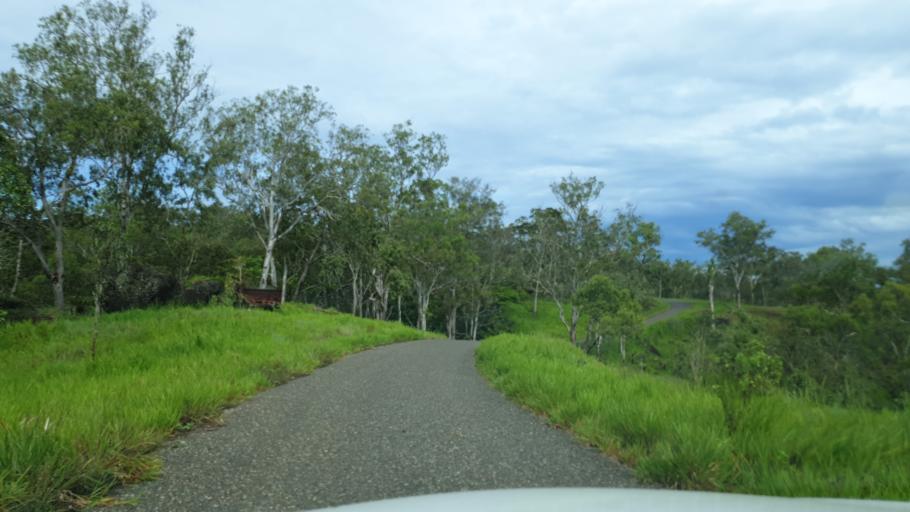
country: PG
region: National Capital
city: Port Moresby
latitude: -9.4352
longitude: 147.3825
